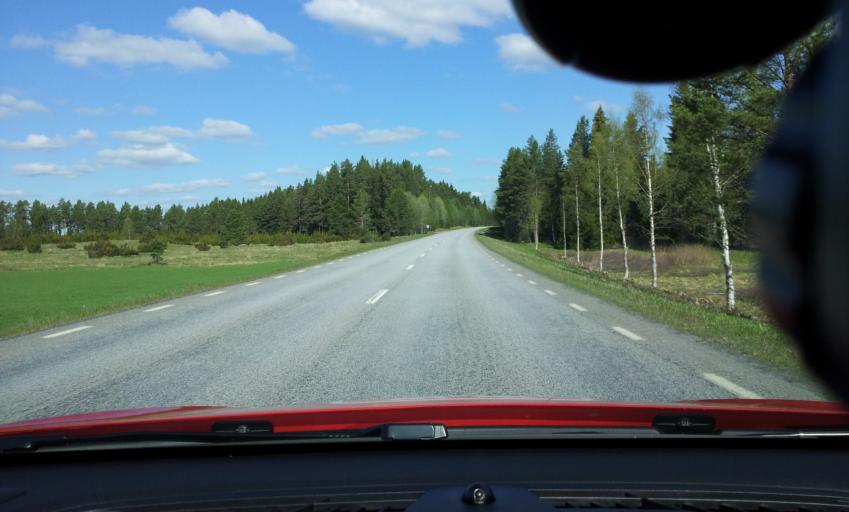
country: SE
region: Jaemtland
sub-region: Krokoms Kommun
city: Valla
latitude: 63.2757
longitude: 13.9412
